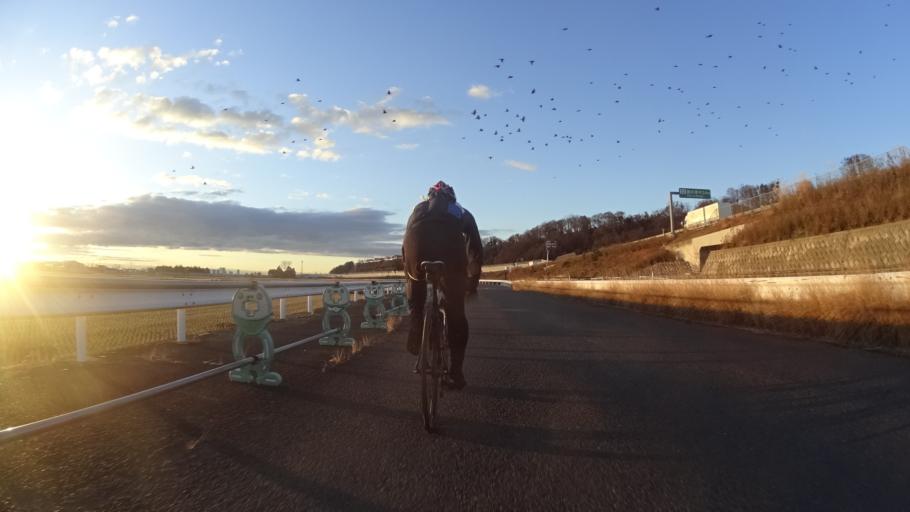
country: JP
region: Kanagawa
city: Zama
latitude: 35.5042
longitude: 139.3665
